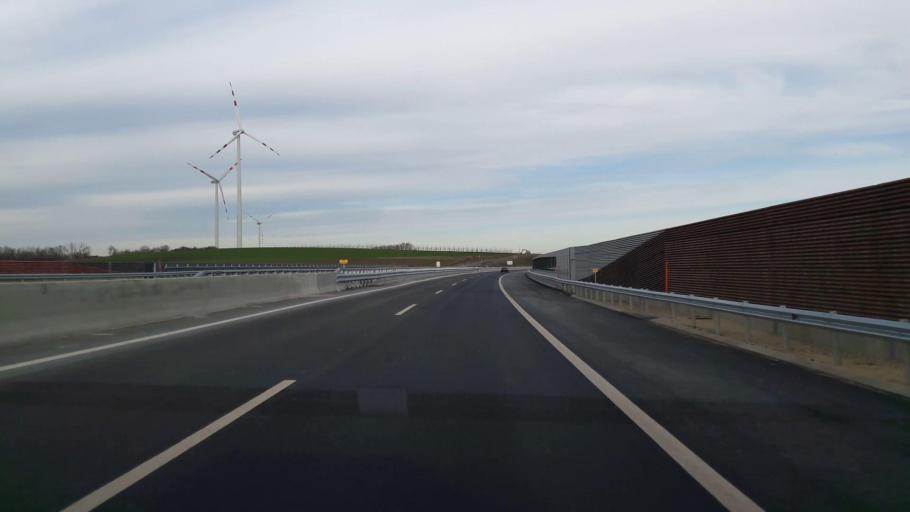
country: AT
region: Lower Austria
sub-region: Politischer Bezirk Mistelbach
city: Wilfersdorf
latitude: 48.5966
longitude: 16.6334
